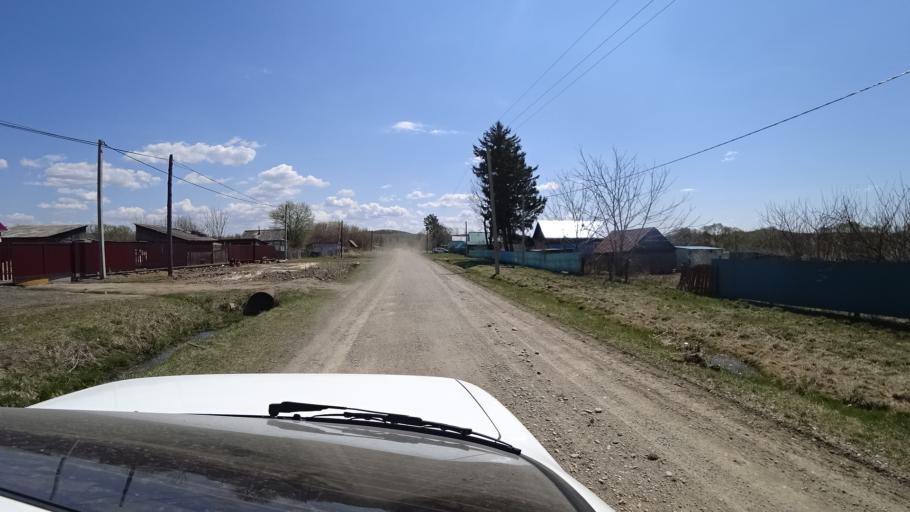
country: RU
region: Primorskiy
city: Lazo
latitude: 45.7924
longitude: 133.7641
